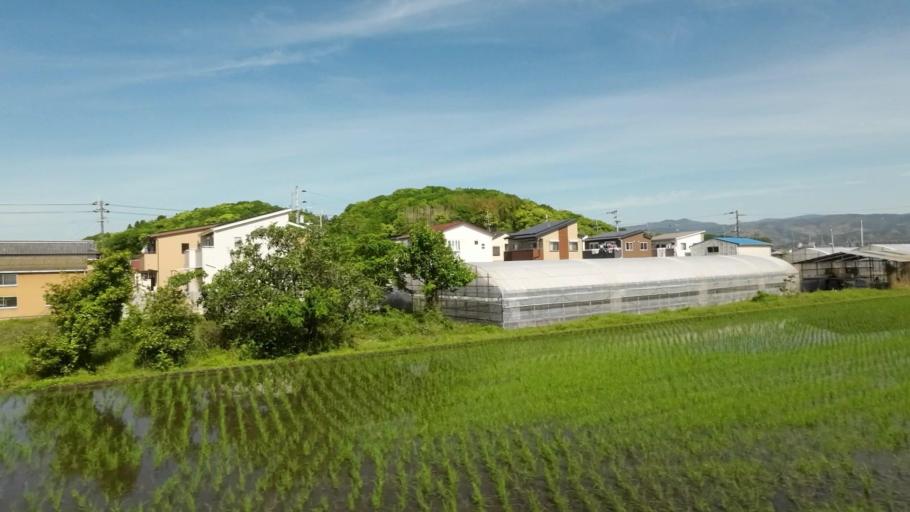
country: JP
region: Kochi
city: Kochi-shi
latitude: 33.5816
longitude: 133.6502
